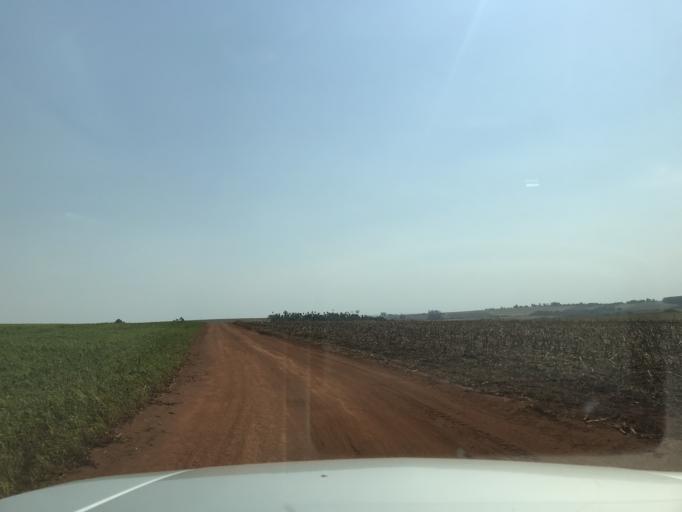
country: BR
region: Parana
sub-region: Palotina
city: Palotina
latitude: -24.2291
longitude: -53.7385
